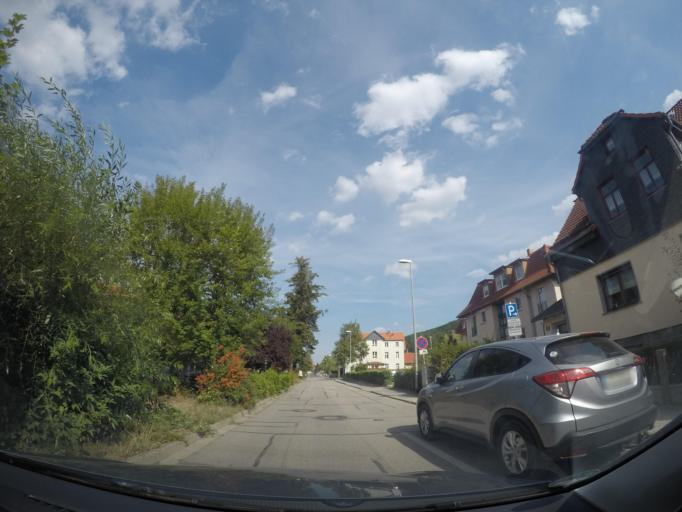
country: DE
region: Saxony-Anhalt
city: Wernigerode
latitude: 51.8197
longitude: 10.7523
